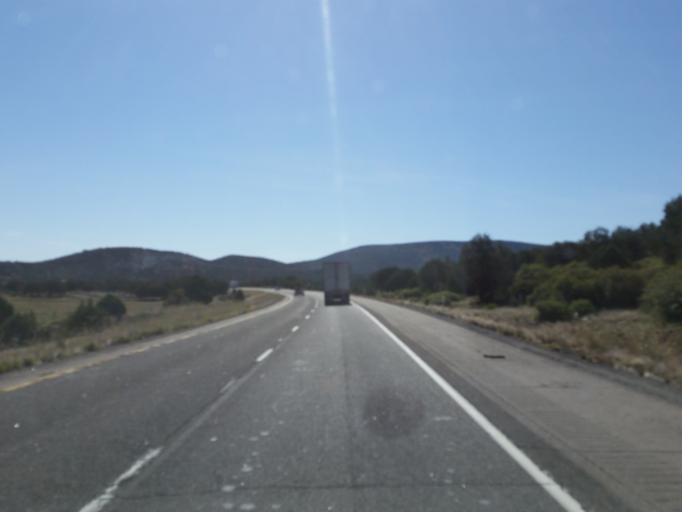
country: US
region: Arizona
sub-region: Mohave County
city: Peach Springs
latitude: 35.1809
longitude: -113.4622
